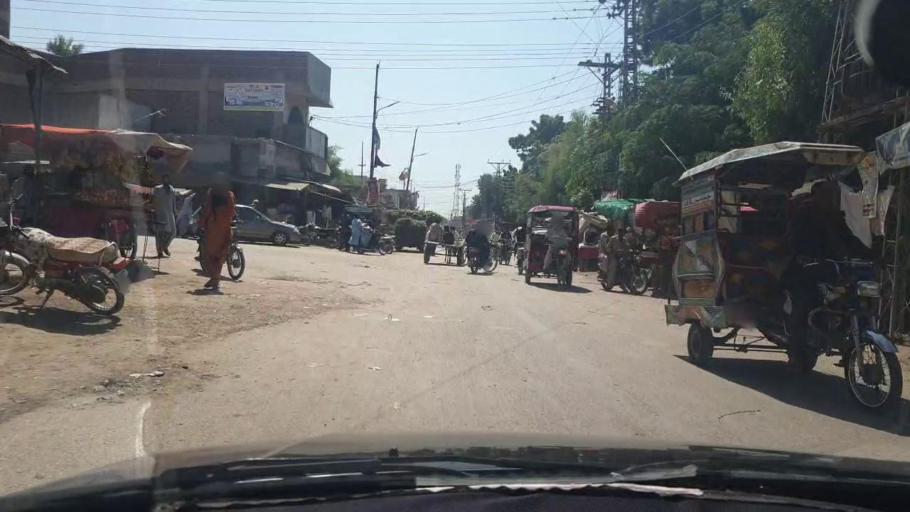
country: PK
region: Sindh
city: Chambar
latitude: 25.2959
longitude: 68.8108
